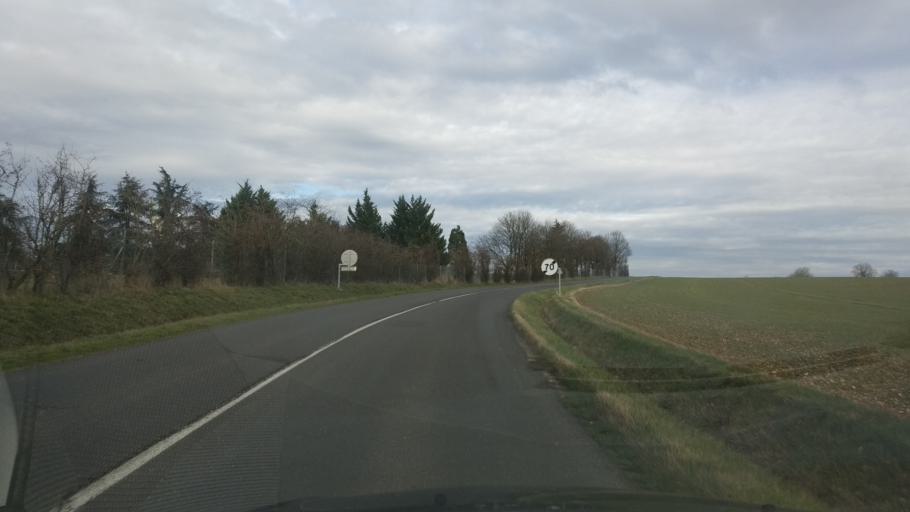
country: FR
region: Poitou-Charentes
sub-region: Departement de la Vienne
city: Saint-Georges-les-Baillargeaux
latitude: 46.6617
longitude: 0.3935
